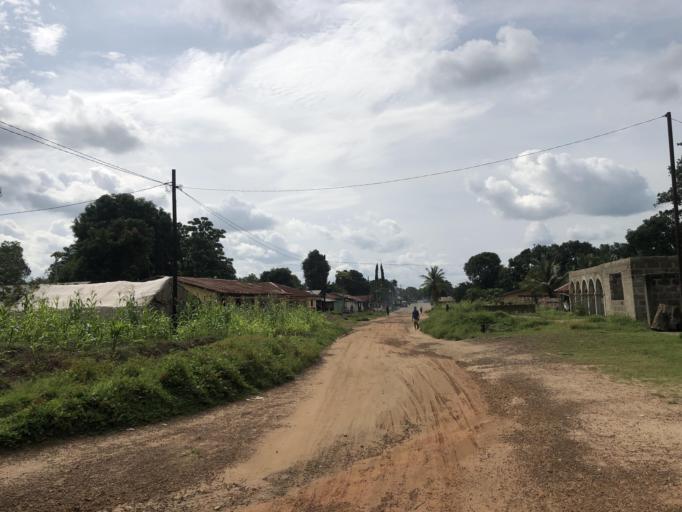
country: SL
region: Northern Province
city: Magburaka
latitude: 8.7135
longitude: -11.9360
